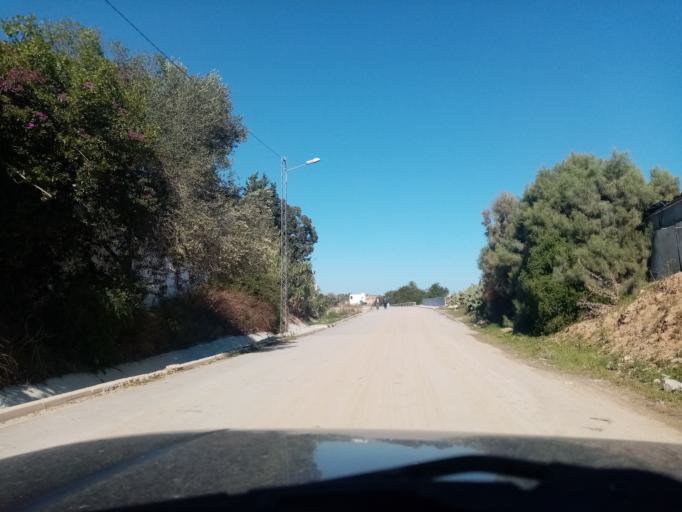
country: TN
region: Nabul
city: Bu `Urqub
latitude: 36.5792
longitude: 10.5706
